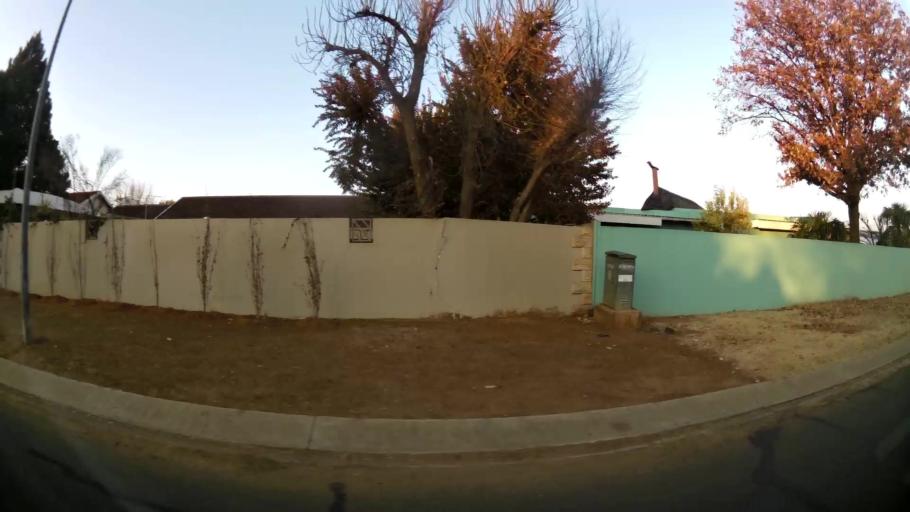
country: ZA
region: Orange Free State
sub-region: Mangaung Metropolitan Municipality
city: Bloemfontein
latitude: -29.1075
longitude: 26.1537
